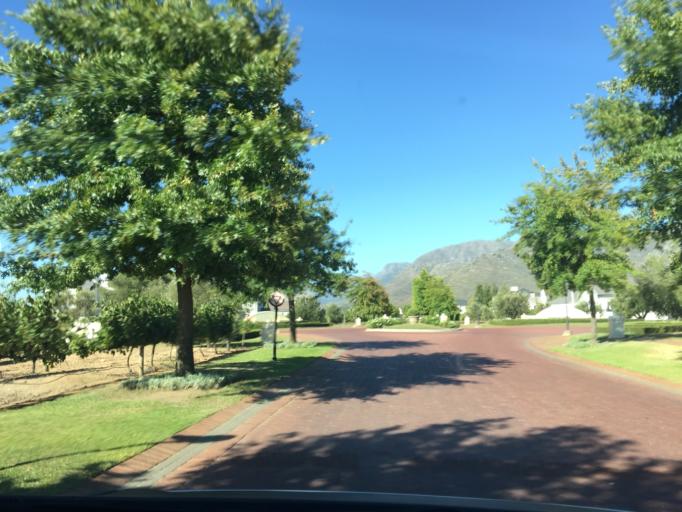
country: ZA
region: Western Cape
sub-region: Cape Winelands District Municipality
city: Paarl
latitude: -33.8026
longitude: 18.9668
